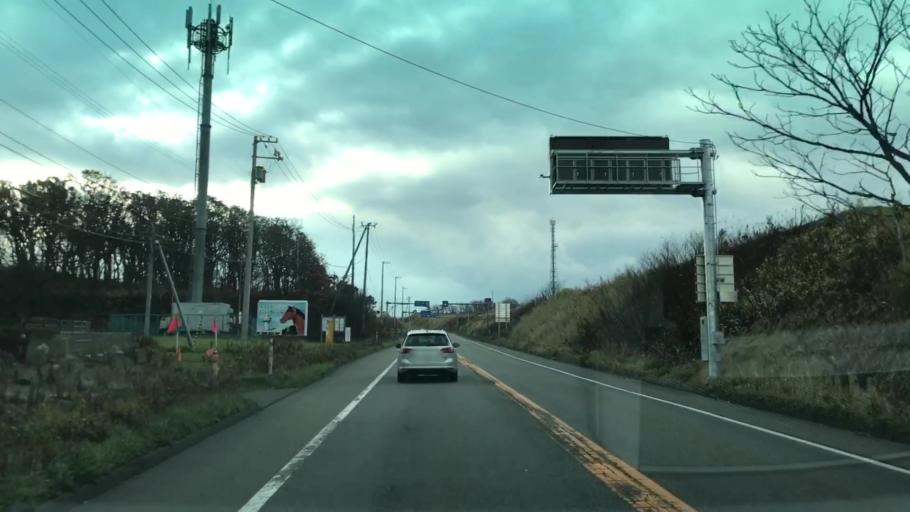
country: JP
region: Hokkaido
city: Shizunai-furukawacho
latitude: 42.4203
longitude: 142.2279
